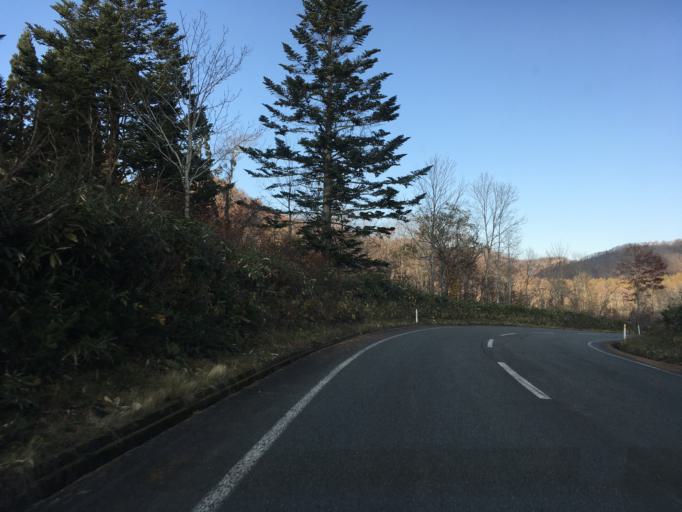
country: JP
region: Akita
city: Yuzawa
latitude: 39.0087
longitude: 140.7347
